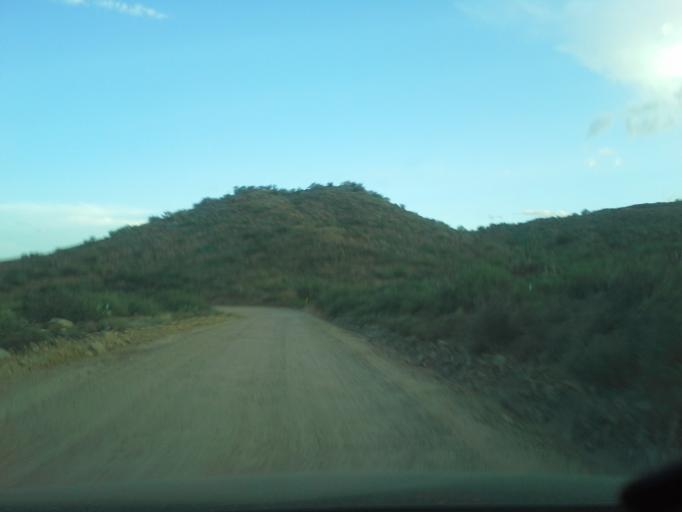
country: US
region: Arizona
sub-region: Yavapai County
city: Cordes Lakes
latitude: 34.2387
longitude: -112.1638
